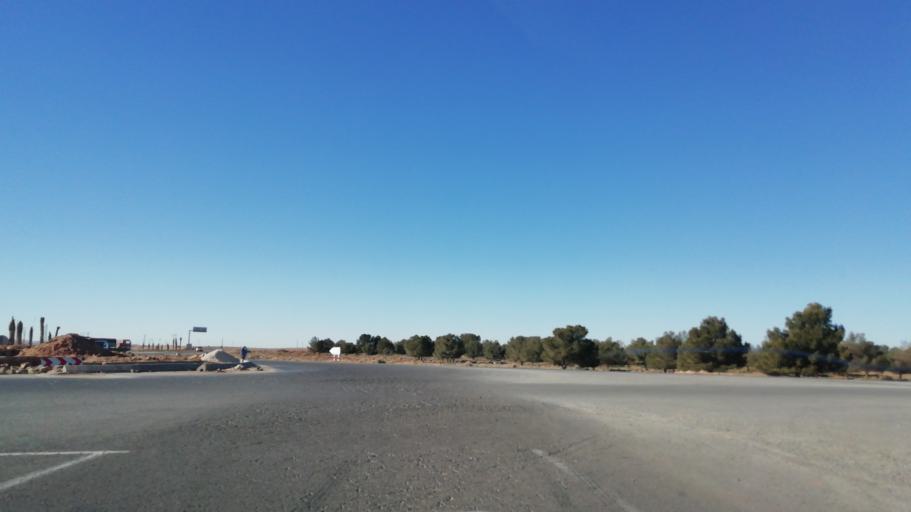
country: DZ
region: El Bayadh
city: El Bayadh
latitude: 33.6570
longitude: 0.9073
